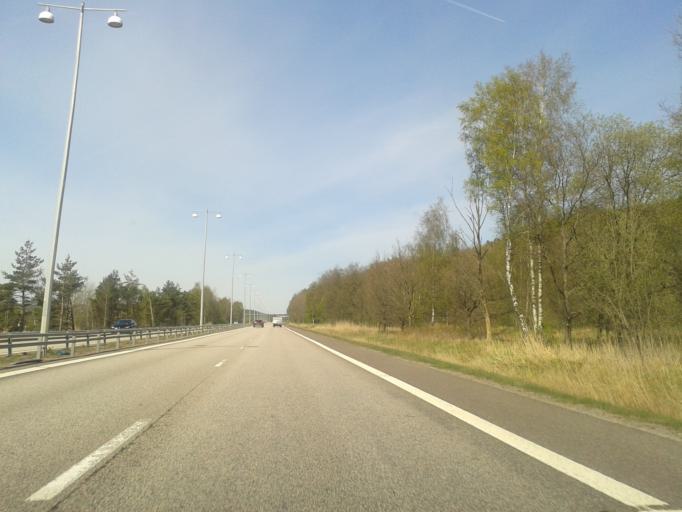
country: SE
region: Vaestra Goetaland
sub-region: Goteborg
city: Hammarkullen
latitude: 57.7737
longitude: 12.0086
